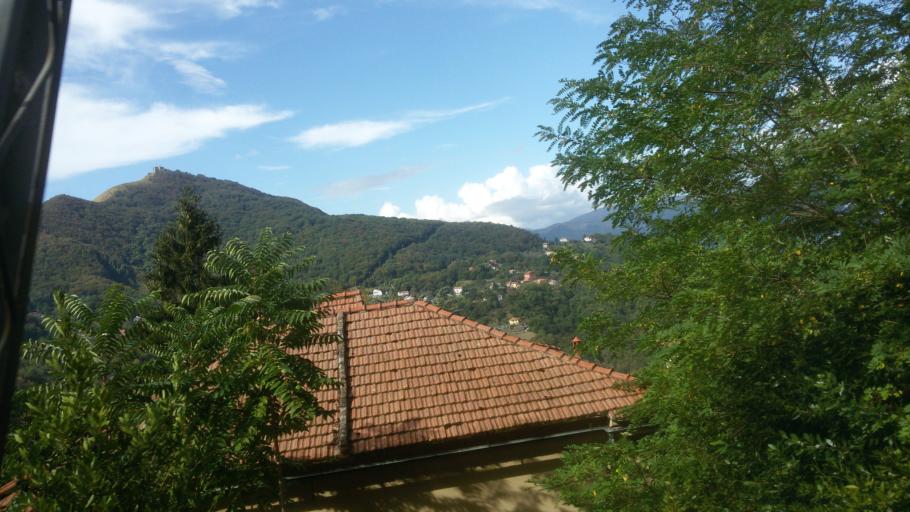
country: IT
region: Liguria
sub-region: Provincia di Genova
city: Piccarello
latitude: 44.4693
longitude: 8.9593
